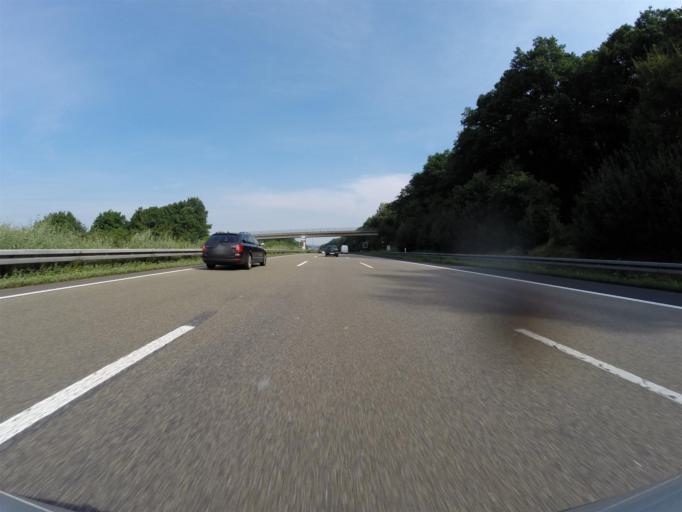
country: DE
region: Hesse
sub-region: Regierungsbezirk Kassel
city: Malsfeld
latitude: 51.0844
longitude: 9.4850
